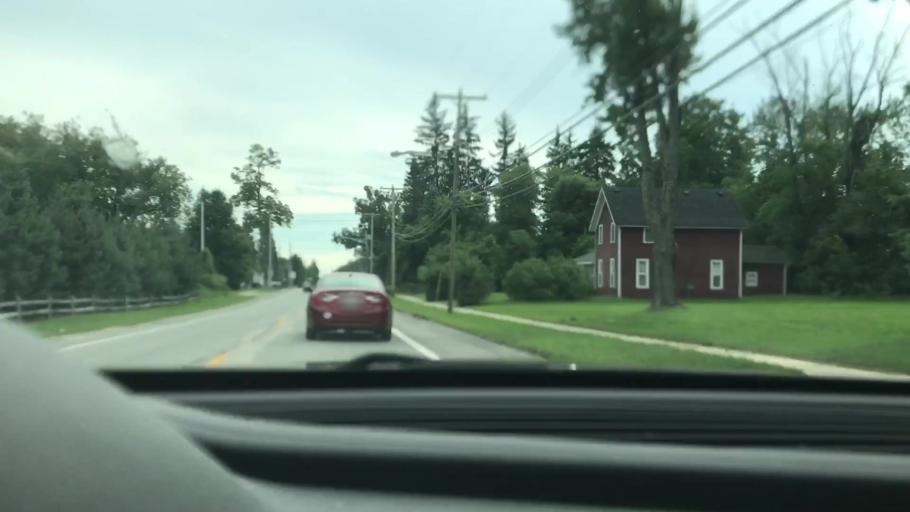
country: US
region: Michigan
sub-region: Antrim County
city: Bellaire
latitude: 45.0743
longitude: -85.2642
